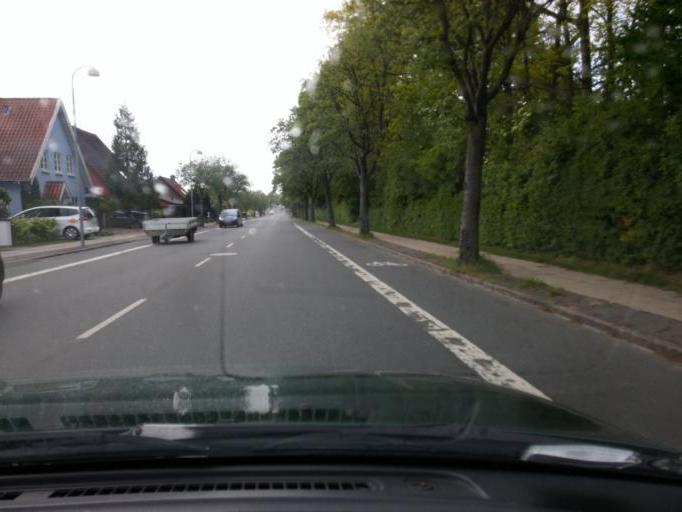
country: DK
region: South Denmark
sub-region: Odense Kommune
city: Odense
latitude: 55.4116
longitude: 10.4071
